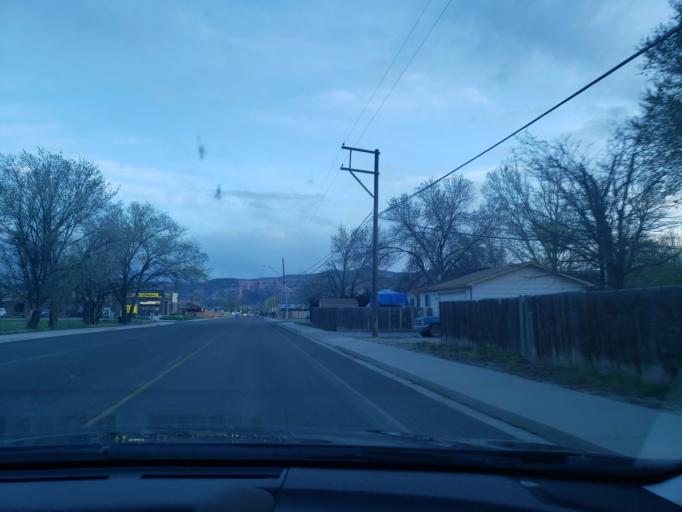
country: US
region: Colorado
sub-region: Mesa County
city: Fruita
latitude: 39.1542
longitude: -108.7198
